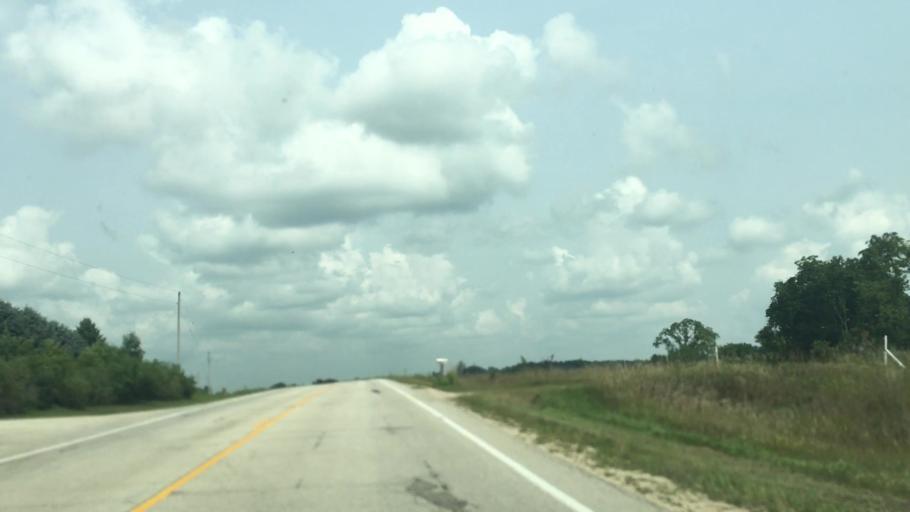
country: US
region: Minnesota
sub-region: Fillmore County
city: Preston
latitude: 43.6828
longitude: -91.9424
